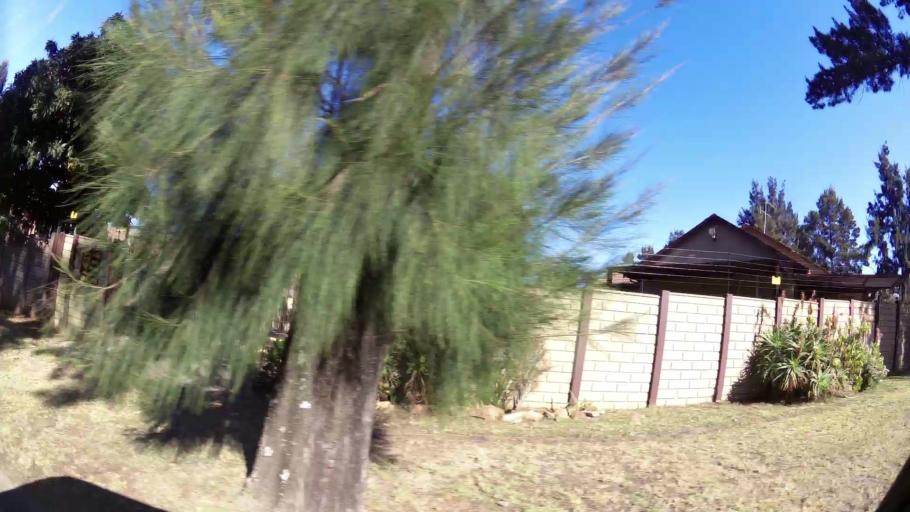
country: ZA
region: Gauteng
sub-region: Ekurhuleni Metropolitan Municipality
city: Germiston
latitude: -26.3385
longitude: 28.1014
